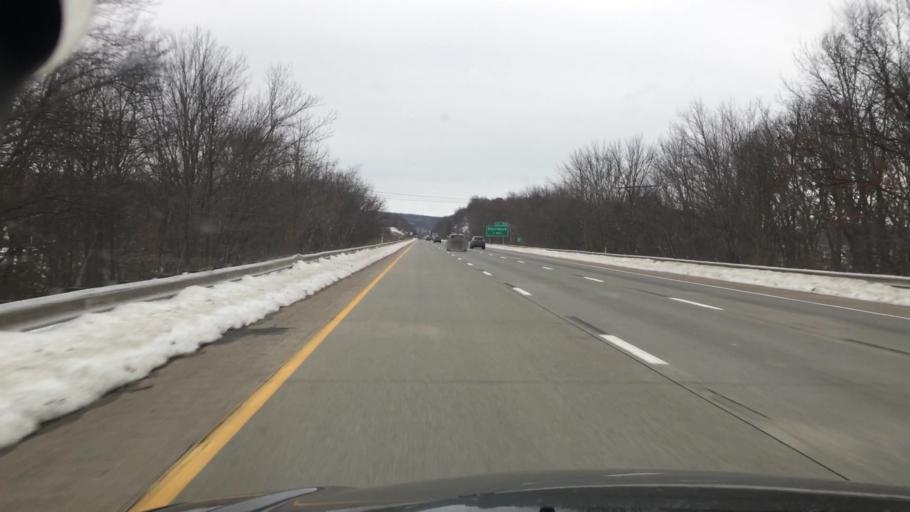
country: US
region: Pennsylvania
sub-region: Luzerne County
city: Freeland
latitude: 41.1012
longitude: -75.9617
